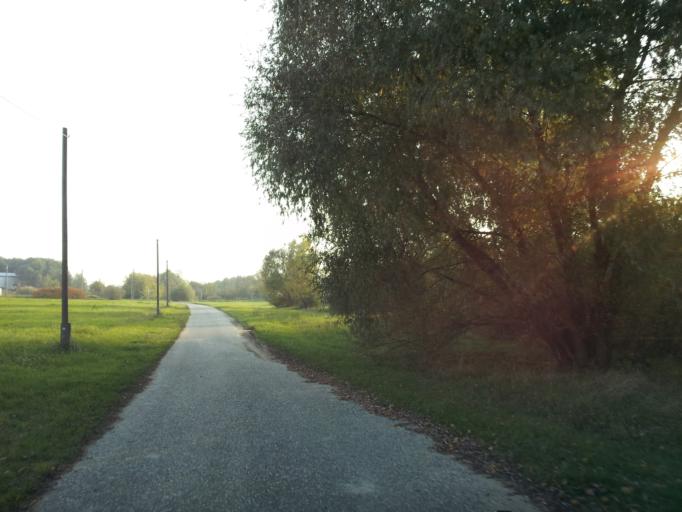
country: HU
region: Komarom-Esztergom
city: Kisber
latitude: 47.5110
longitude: 18.0092
